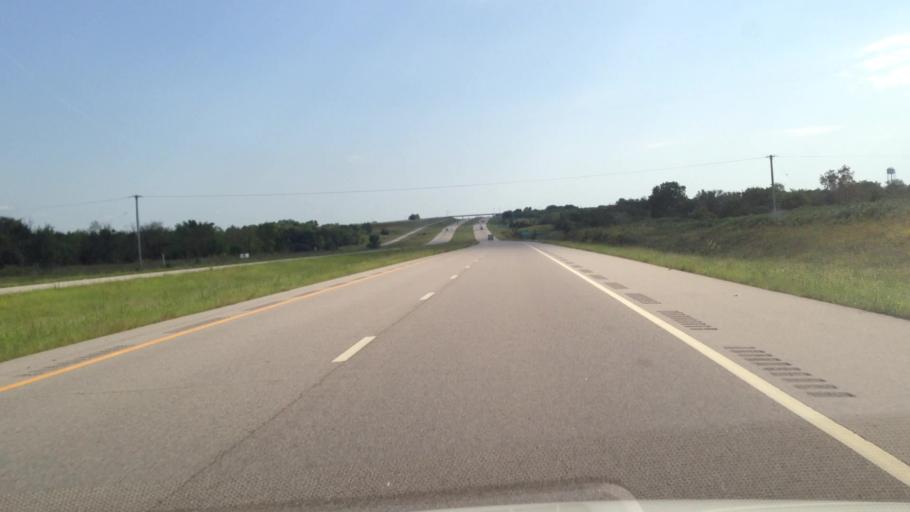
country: US
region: Kansas
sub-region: Linn County
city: La Cygne
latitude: 38.4194
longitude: -94.6878
